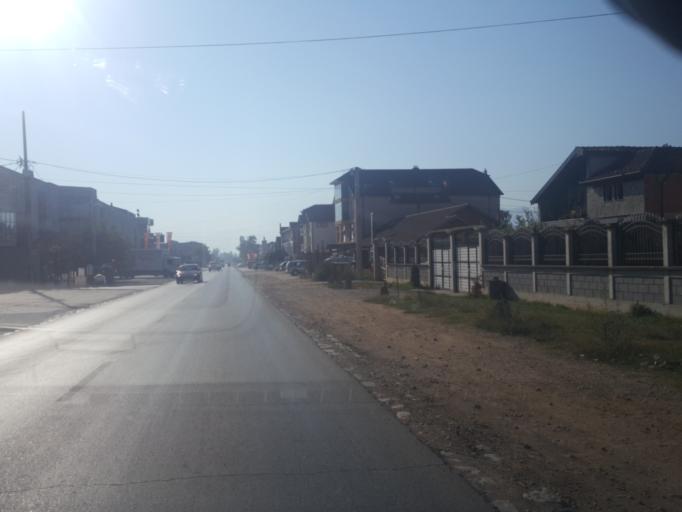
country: XK
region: Gjakova
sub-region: Komuna e Gjakoves
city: Gjakove
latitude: 42.4072
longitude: 20.4076
